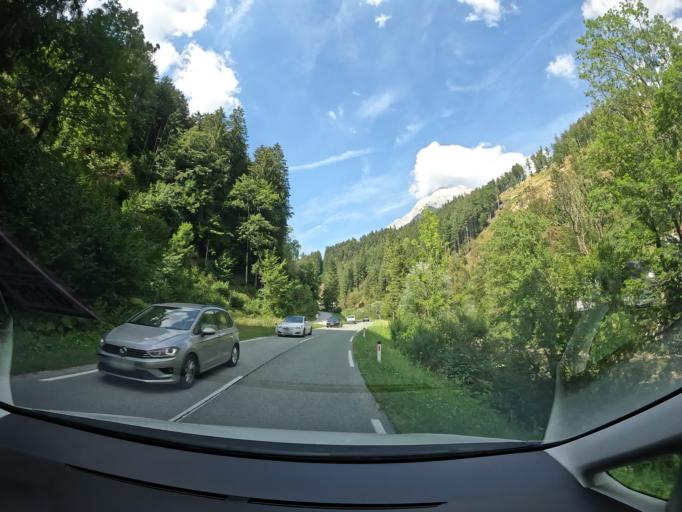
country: SI
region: Cerklje na Gorenjskem
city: Cerklje na Gorenjskem
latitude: 46.3234
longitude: 14.4933
